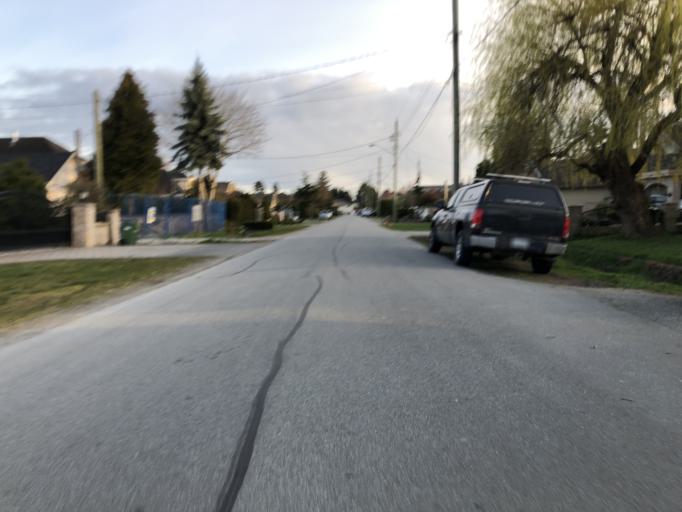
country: CA
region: British Columbia
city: Richmond
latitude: 49.1505
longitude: -123.1270
